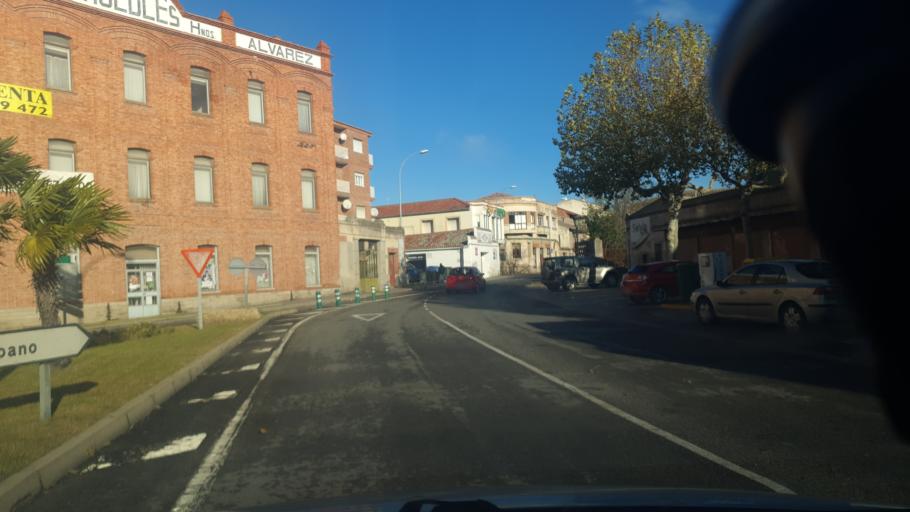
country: ES
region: Castille and Leon
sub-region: Provincia de Avila
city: Arevalo
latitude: 41.0596
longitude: -4.7205
